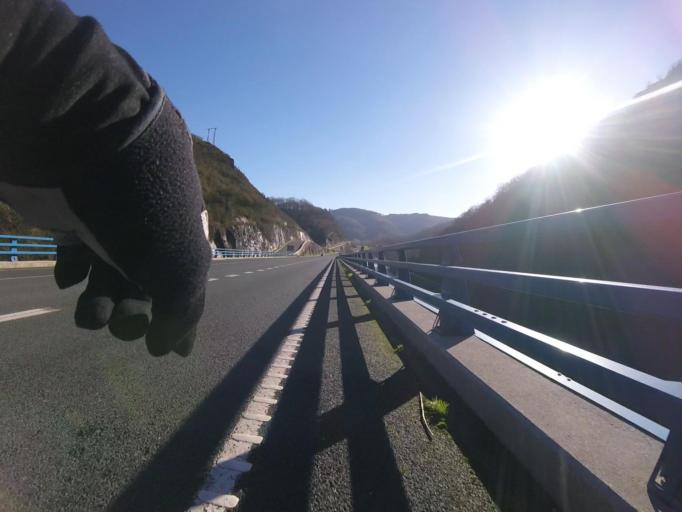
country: ES
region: Navarre
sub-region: Provincia de Navarra
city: Bera
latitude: 43.2884
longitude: -1.7115
